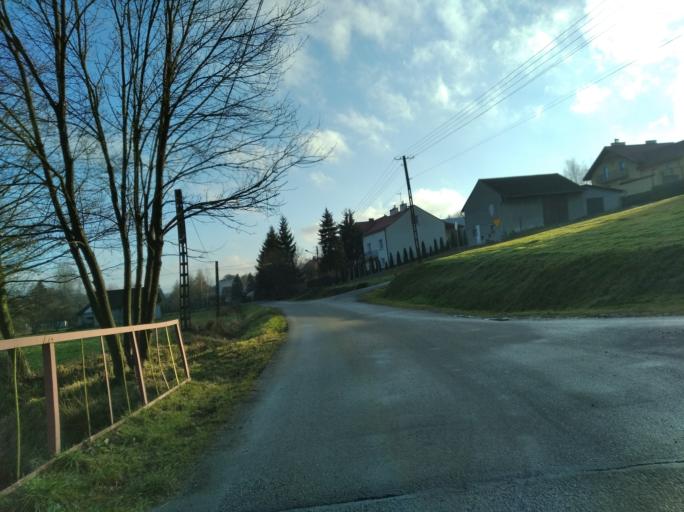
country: PL
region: Subcarpathian Voivodeship
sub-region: Powiat strzyzowski
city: Czudec
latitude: 49.9479
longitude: 21.8042
